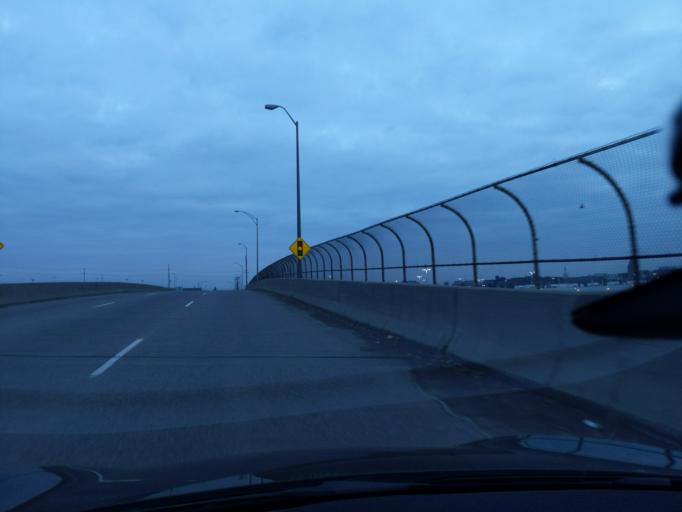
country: US
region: Michigan
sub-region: Ingham County
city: Lansing
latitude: 42.7208
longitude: -84.5673
